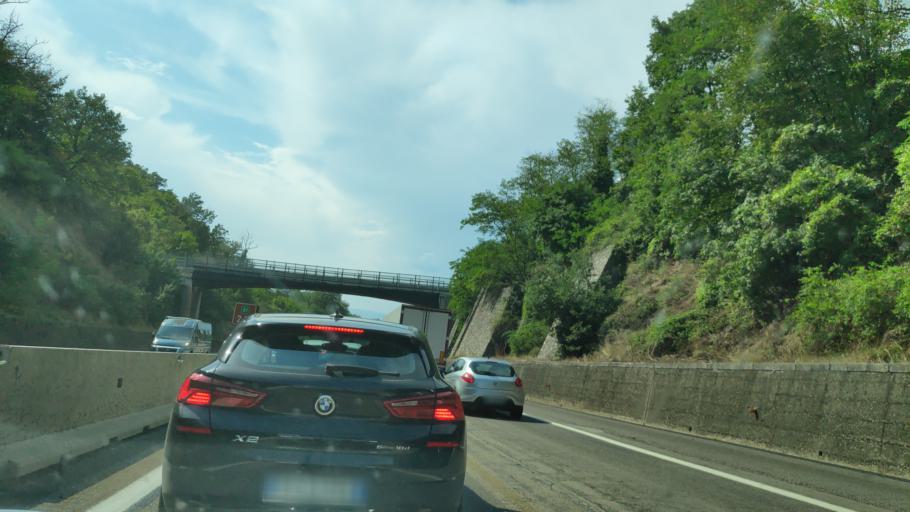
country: IT
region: Tuscany
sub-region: Province of Arezzo
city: Montalto
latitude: 43.5131
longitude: 11.6414
